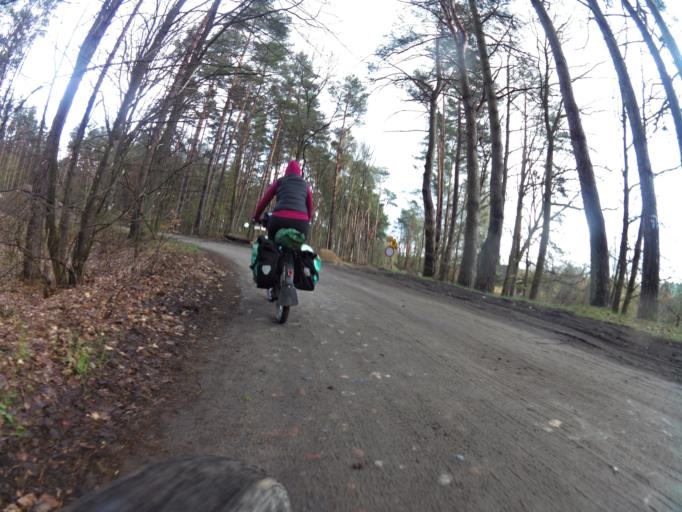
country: PL
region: Pomeranian Voivodeship
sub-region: Powiat slupski
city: Kepice
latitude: 54.2849
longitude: 16.8285
